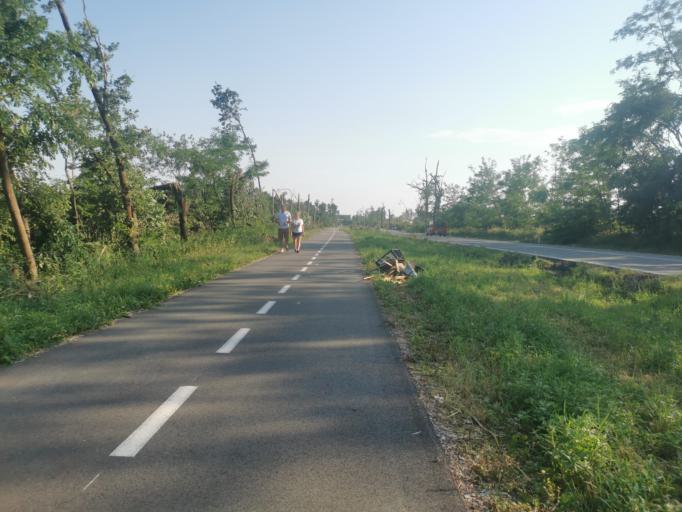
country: CZ
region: South Moravian
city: Rohatec
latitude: 48.8882
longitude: 17.1496
